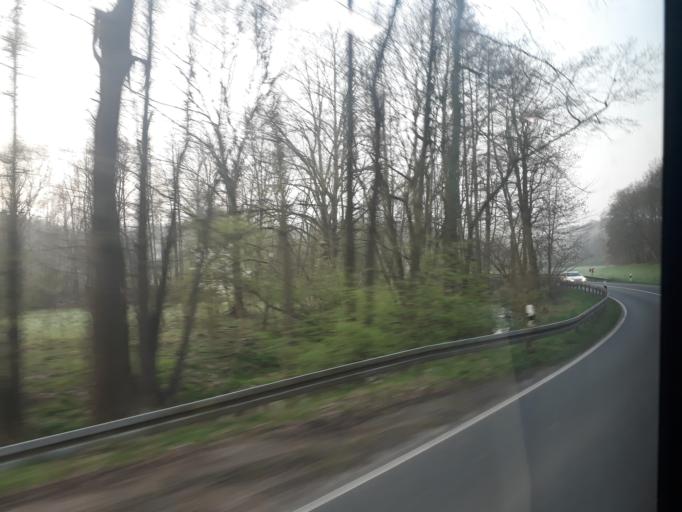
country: DE
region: Saxony
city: Kreischa
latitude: 50.9712
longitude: 13.7779
